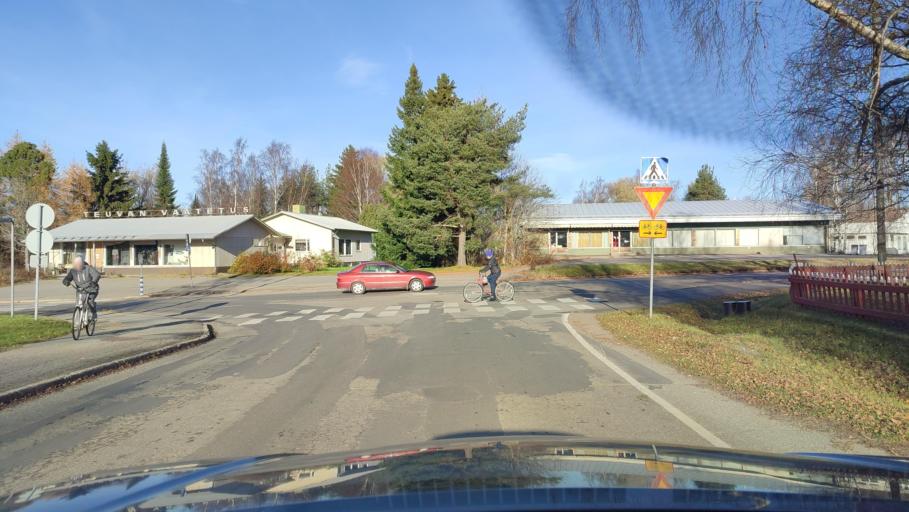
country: FI
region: Southern Ostrobothnia
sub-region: Suupohja
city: Teuva
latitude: 62.4862
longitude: 21.7502
